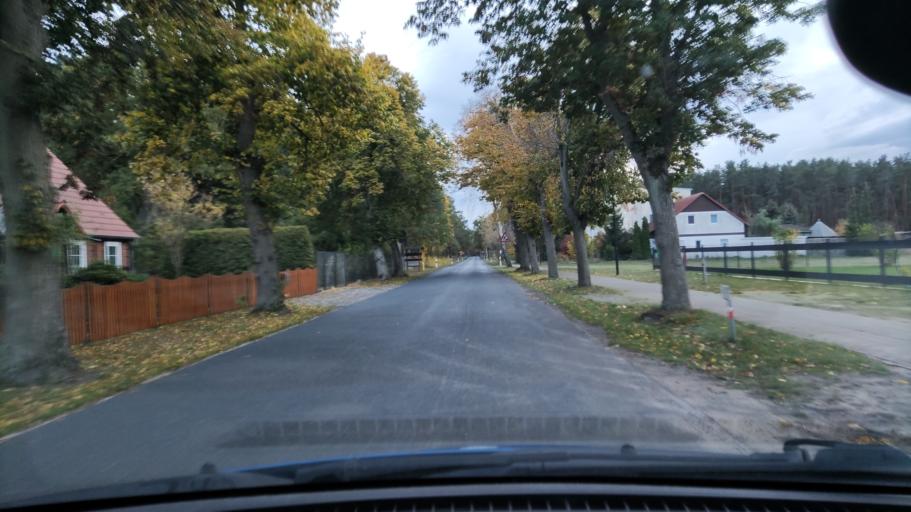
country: DE
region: Saxony-Anhalt
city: Luftkurort Arendsee
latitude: 52.9111
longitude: 11.4924
